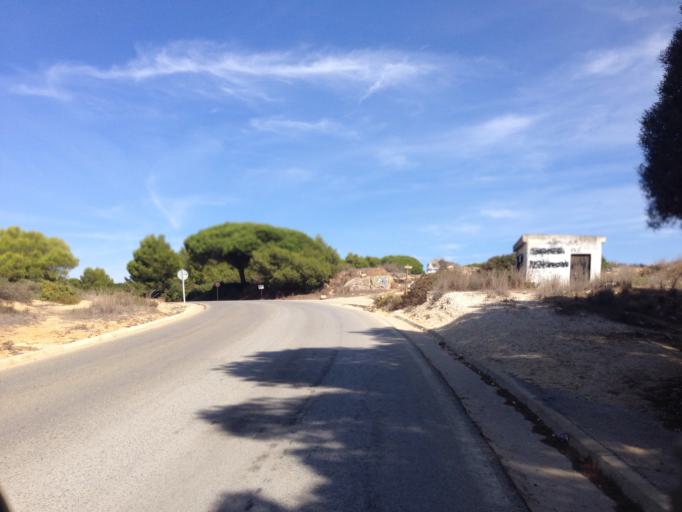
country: ES
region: Andalusia
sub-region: Provincia de Cadiz
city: Conil de la Frontera
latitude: 36.2975
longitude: -6.1371
